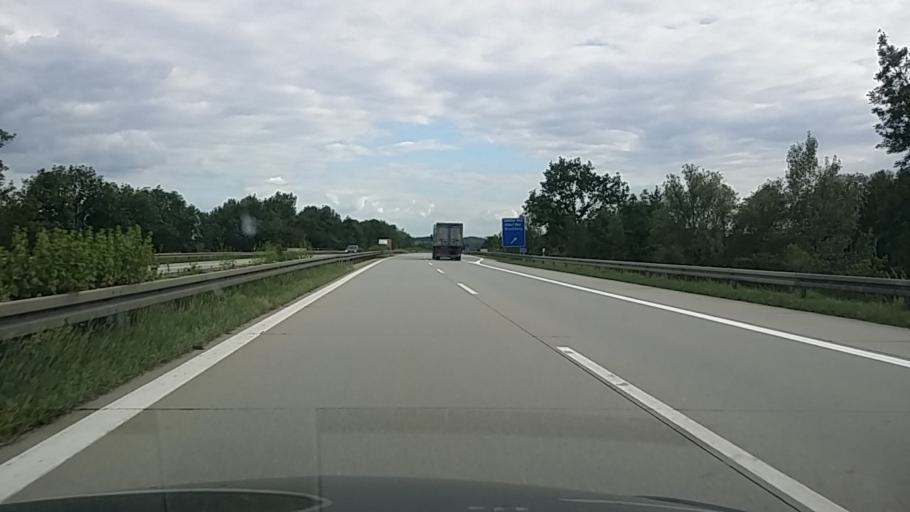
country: DE
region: Bavaria
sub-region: Lower Bavaria
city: Eching
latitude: 48.5377
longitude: 12.0719
